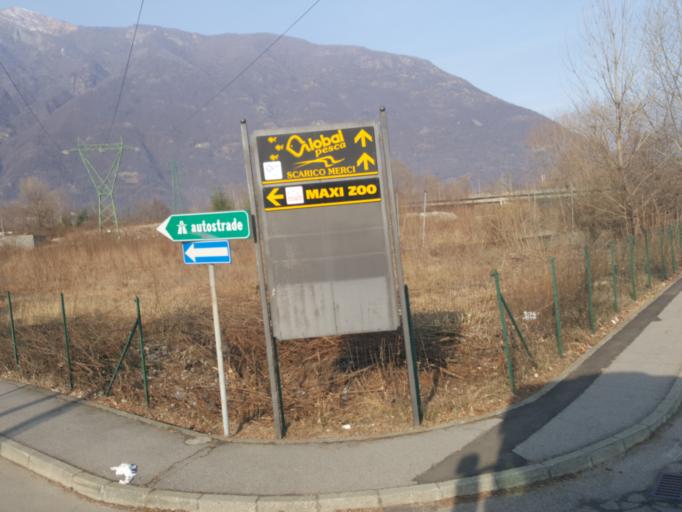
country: IT
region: Piedmont
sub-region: Provincia Verbano-Cusio-Ossola
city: Gravellona Toce
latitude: 45.9316
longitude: 8.4471
